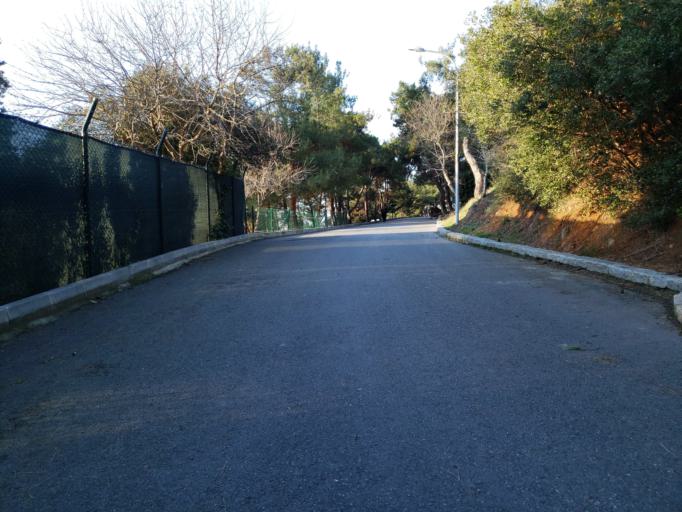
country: TR
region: Istanbul
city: Adalan
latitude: 40.8815
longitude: 29.0915
